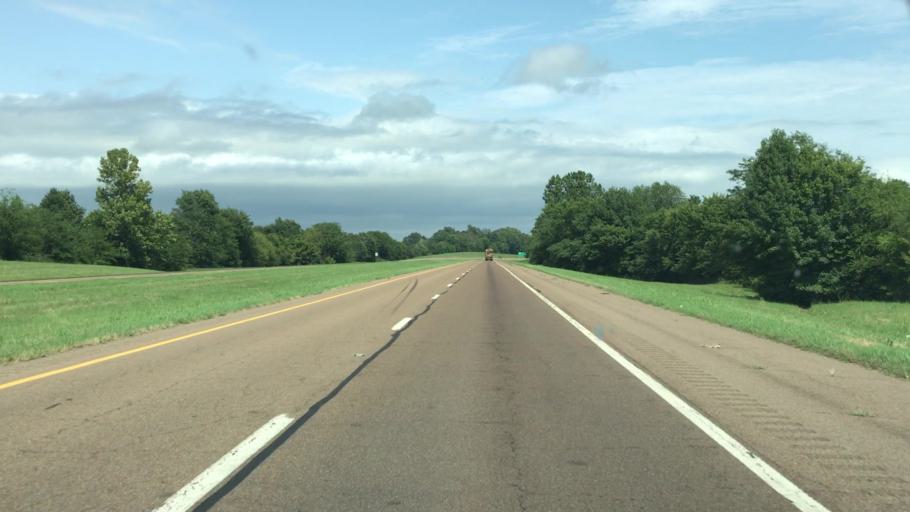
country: US
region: Tennessee
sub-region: Obion County
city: South Fulton
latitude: 36.4921
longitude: -88.9194
